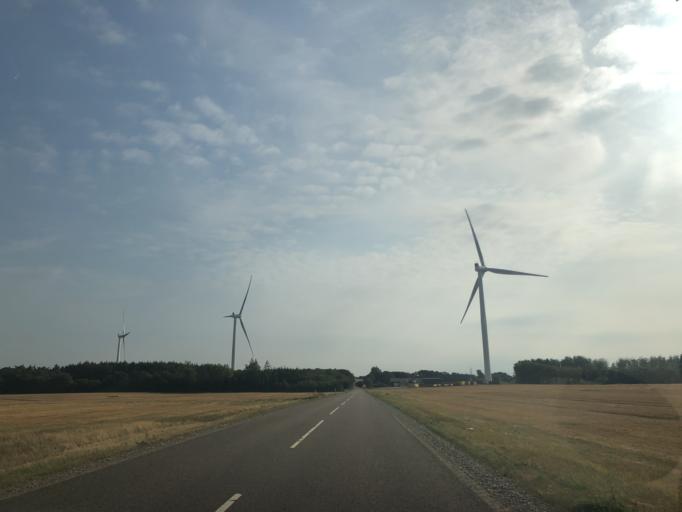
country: DK
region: Central Jutland
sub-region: Skive Kommune
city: Skive
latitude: 56.6859
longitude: 8.9738
